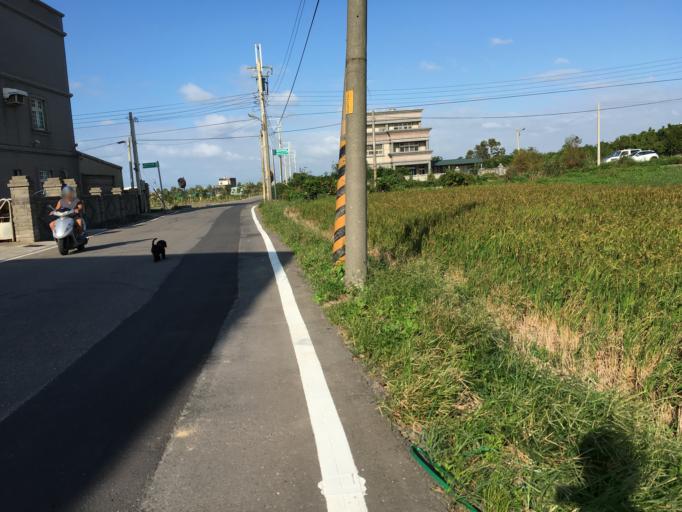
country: TW
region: Taiwan
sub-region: Hsinchu
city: Zhubei
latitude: 24.9285
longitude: 120.9860
